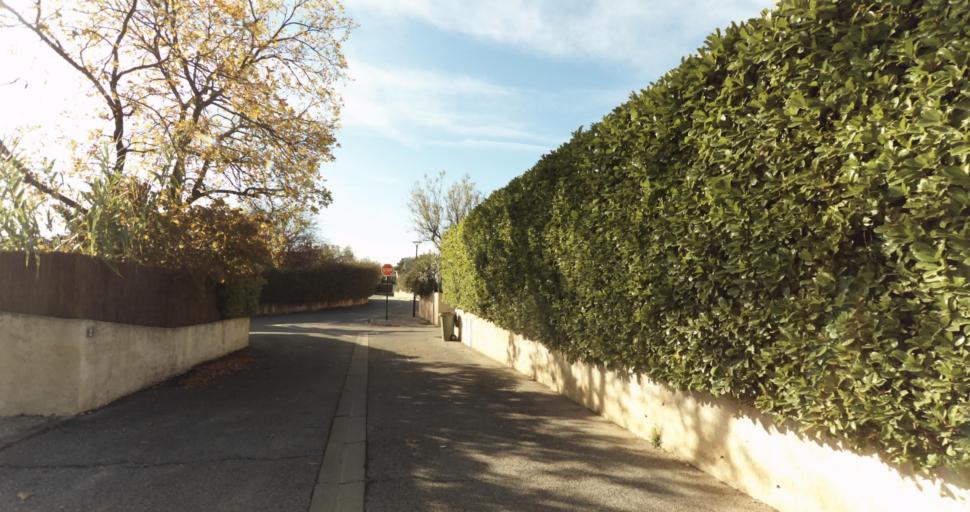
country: FR
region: Provence-Alpes-Cote d'Azur
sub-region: Departement des Bouches-du-Rhone
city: Venelles
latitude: 43.5963
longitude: 5.4706
